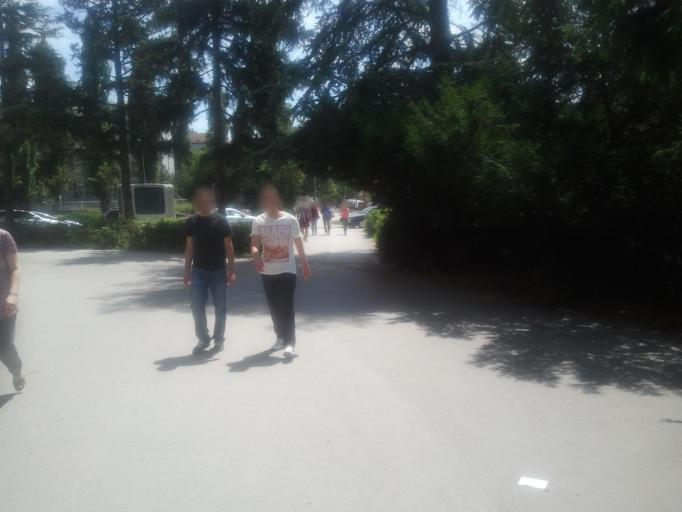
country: RS
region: Autonomna Pokrajina Vojvodina
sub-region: Juznobacki Okrug
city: Novi Sad
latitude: 45.2534
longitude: 19.8480
